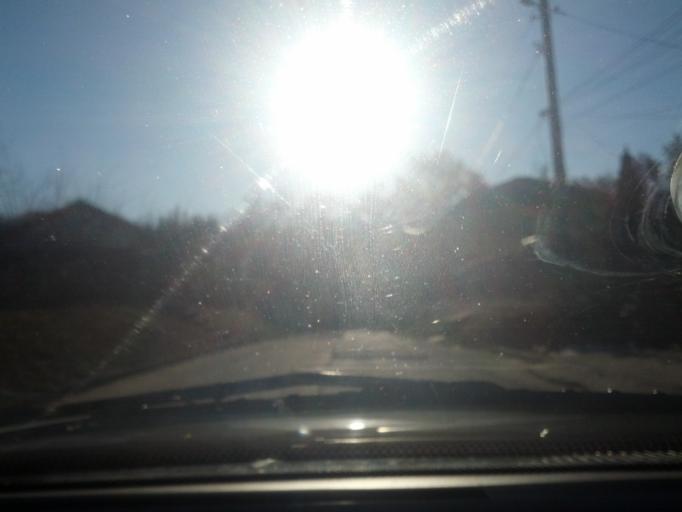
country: BG
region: Vratsa
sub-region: Obshtina Kozloduy
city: Kozloduy
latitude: 43.7880
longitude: 23.7140
